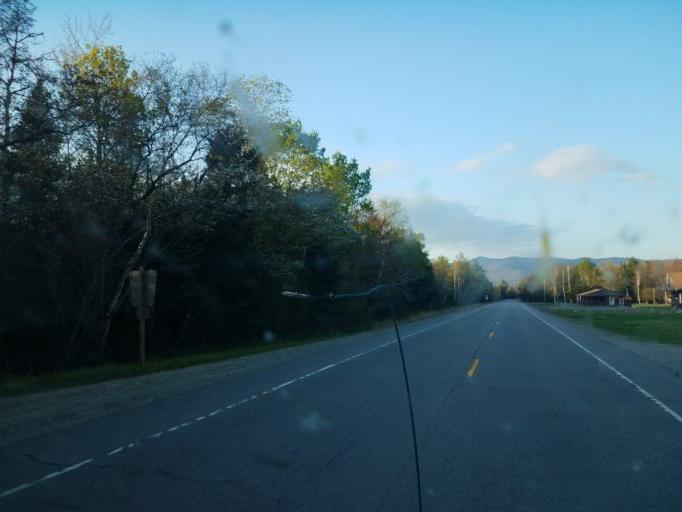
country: US
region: New Hampshire
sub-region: Grafton County
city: Deerfield
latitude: 44.2601
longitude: -71.5819
